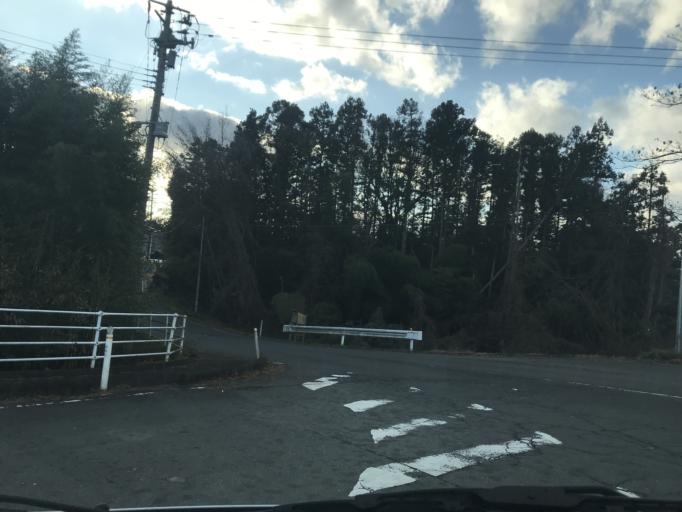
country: JP
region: Miyagi
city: Kogota
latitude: 38.6367
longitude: 141.0697
